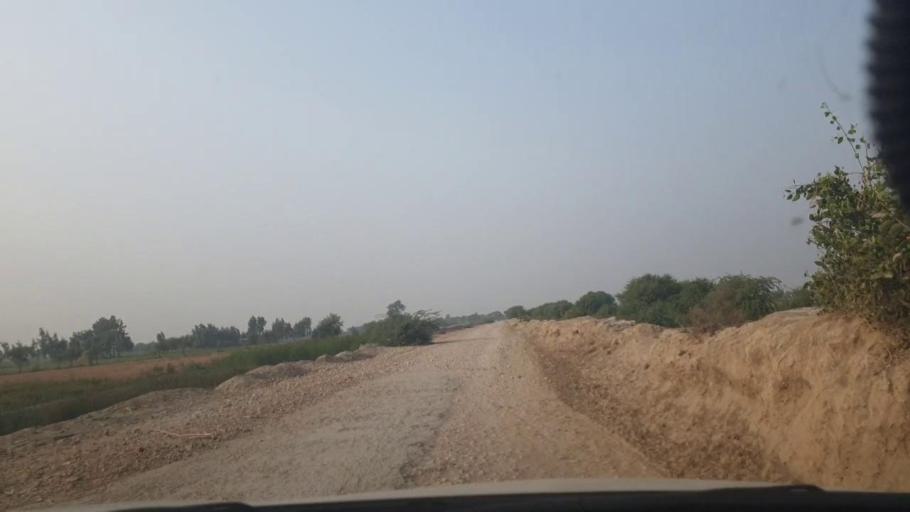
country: PK
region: Sindh
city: Bulri
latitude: 24.7972
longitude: 68.4156
